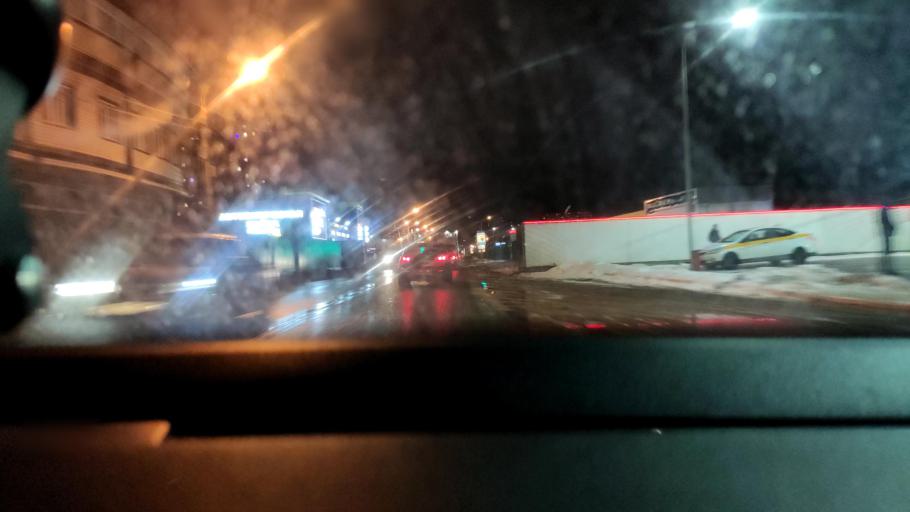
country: RU
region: Moskovskaya
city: Zhukovskiy
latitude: 55.5929
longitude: 38.0970
